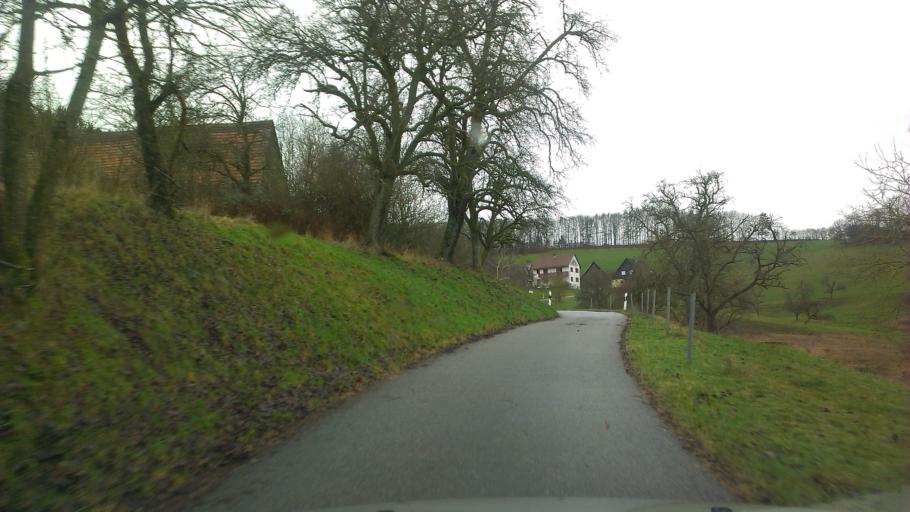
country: DE
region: Baden-Wuerttemberg
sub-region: Karlsruhe Region
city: Heiligkreuzsteinach
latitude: 49.4845
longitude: 8.7792
